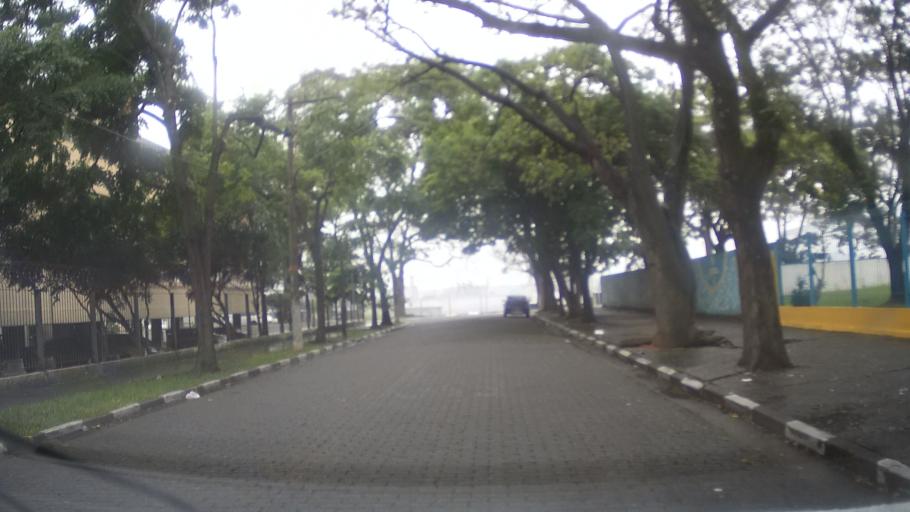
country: BR
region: Sao Paulo
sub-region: Guarulhos
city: Guarulhos
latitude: -23.4624
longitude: -46.4955
